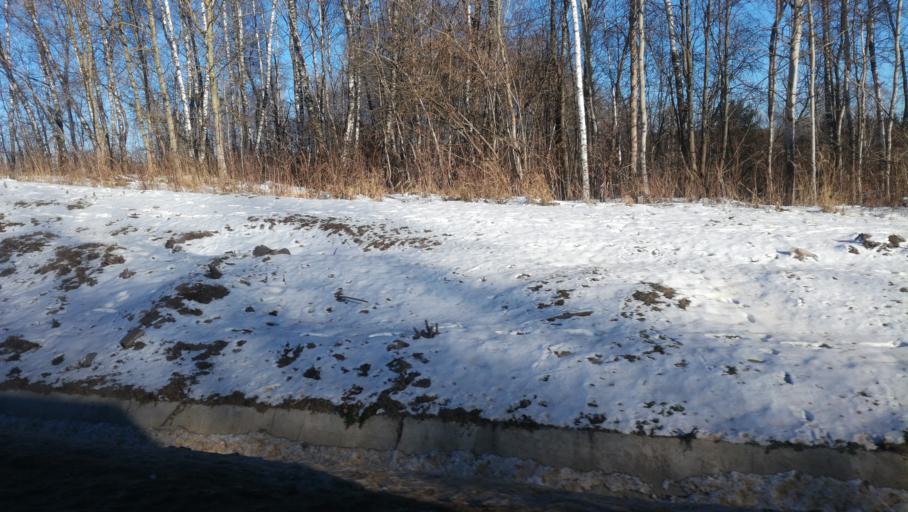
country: RU
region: Tula
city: Kosaya Gora
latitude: 54.1679
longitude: 37.4611
